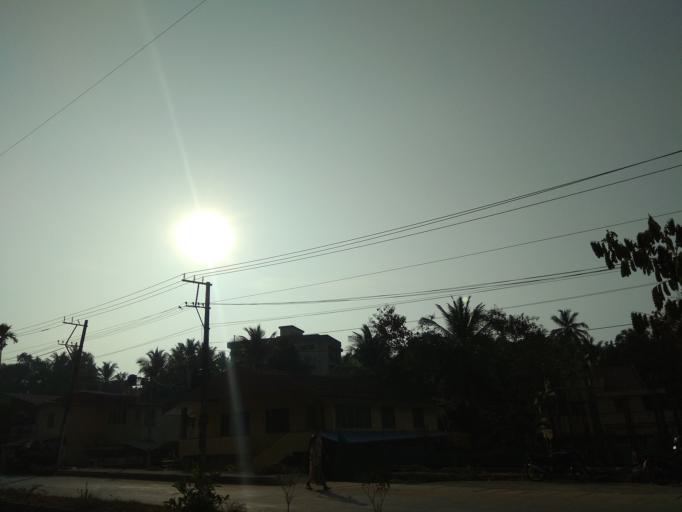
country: IN
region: Karnataka
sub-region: Dakshina Kannada
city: Mangalore
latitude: 12.9016
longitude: 74.8450
